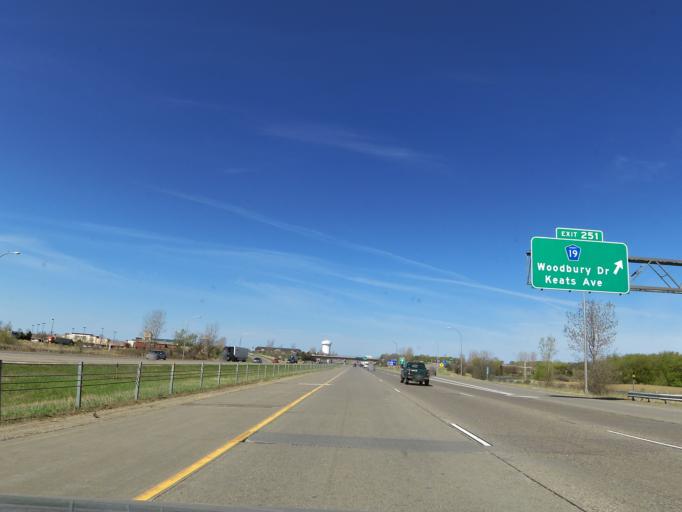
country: US
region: Minnesota
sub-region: Washington County
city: Lake Elmo
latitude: 44.9489
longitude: -92.8951
